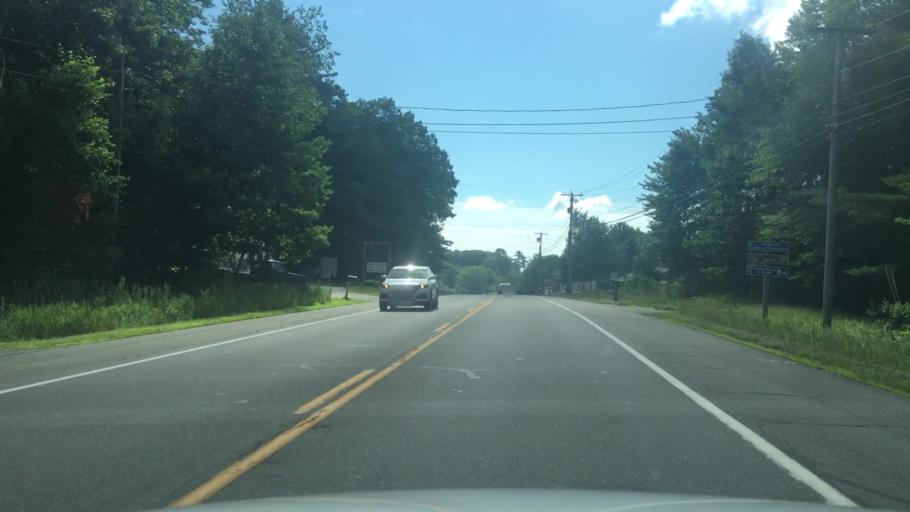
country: US
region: Maine
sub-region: Knox County
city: Warren
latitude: 44.1175
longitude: -69.2681
